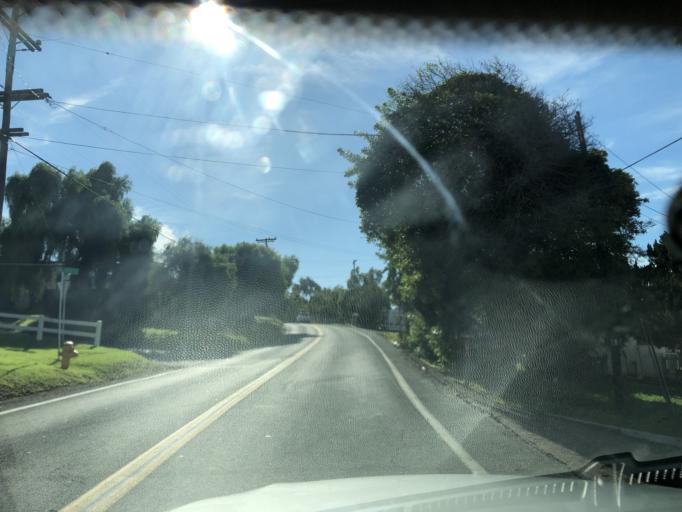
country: US
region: California
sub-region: San Diego County
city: Chula Vista
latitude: 32.6456
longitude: -117.0617
